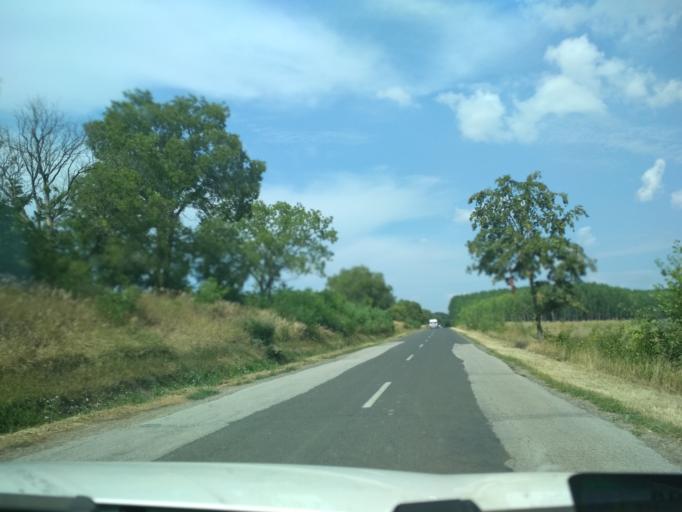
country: HU
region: Jasz-Nagykun-Szolnok
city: Abadszalok
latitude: 47.5134
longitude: 20.6530
